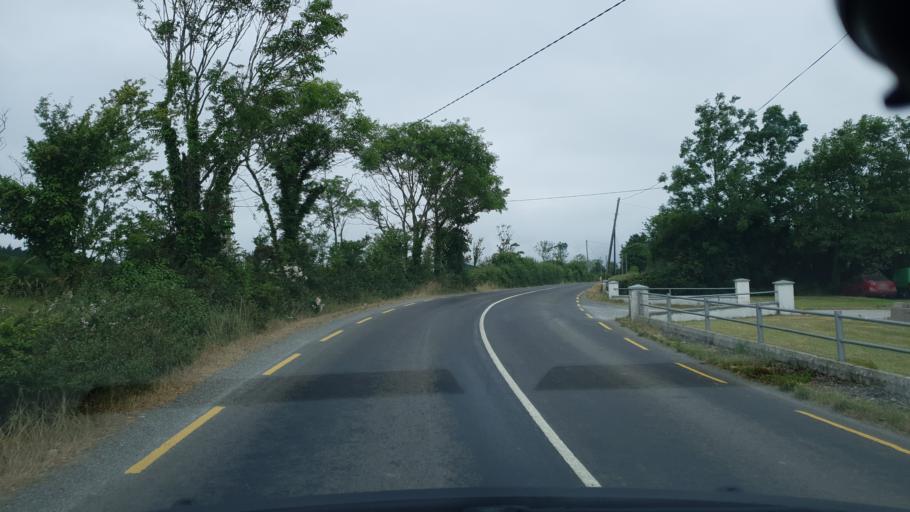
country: IE
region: Munster
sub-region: Ciarrai
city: Tralee
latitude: 52.1584
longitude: -9.6743
